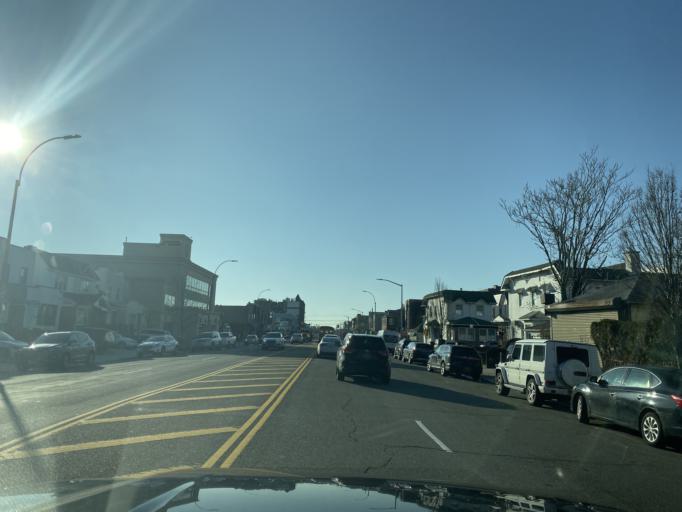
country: US
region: New York
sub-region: Kings County
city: Bensonhurst
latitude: 40.6023
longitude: -73.9615
